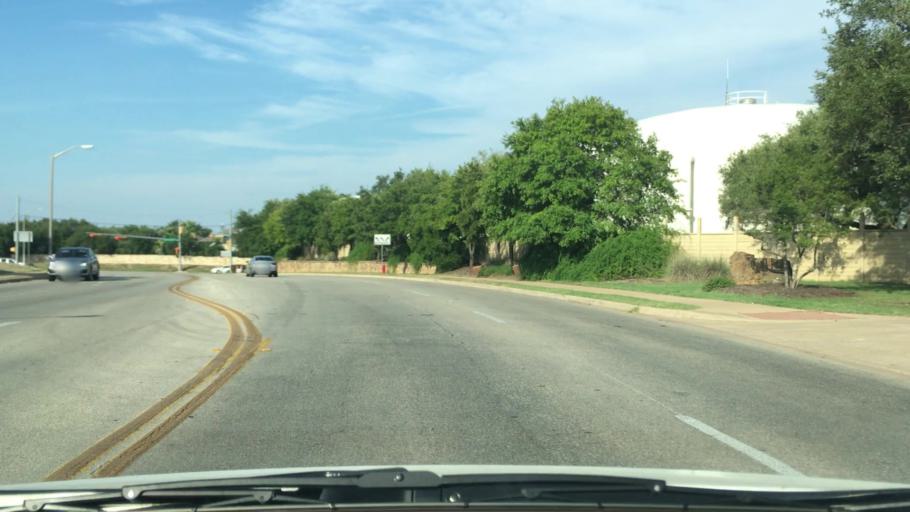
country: US
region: Texas
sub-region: Williamson County
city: Cedar Park
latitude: 30.4733
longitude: -97.8467
